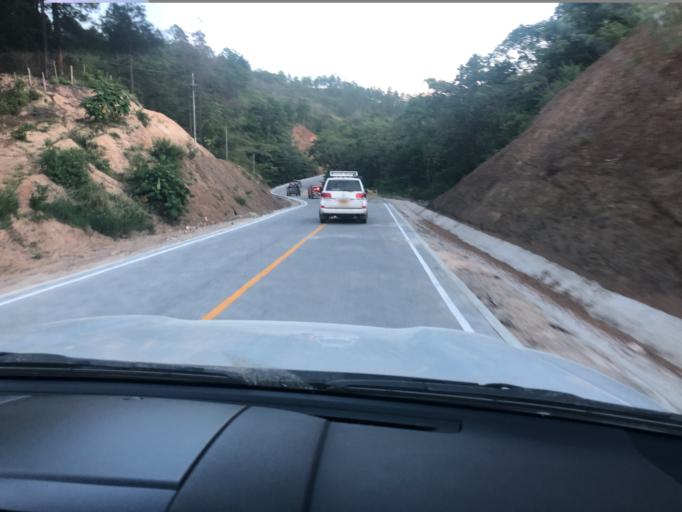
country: NI
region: Nueva Segovia
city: Ocotal
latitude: 13.6727
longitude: -86.6155
